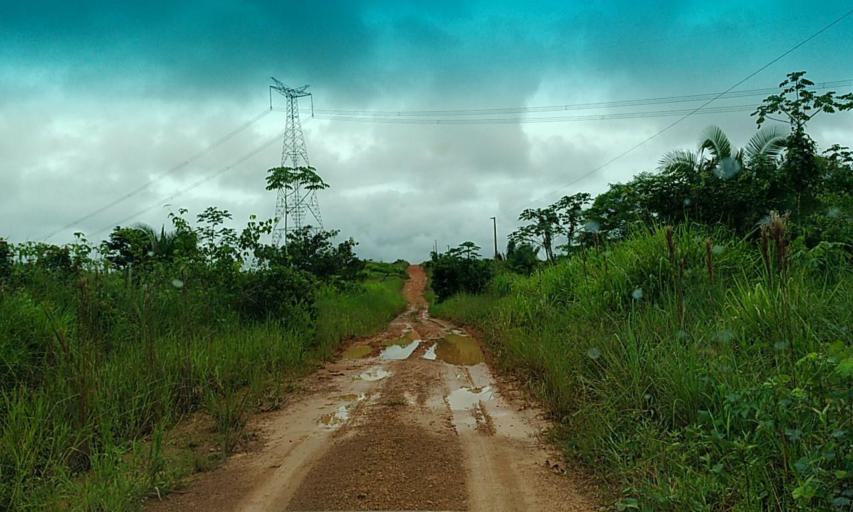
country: BR
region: Para
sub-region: Altamira
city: Altamira
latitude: -3.1192
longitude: -51.6028
